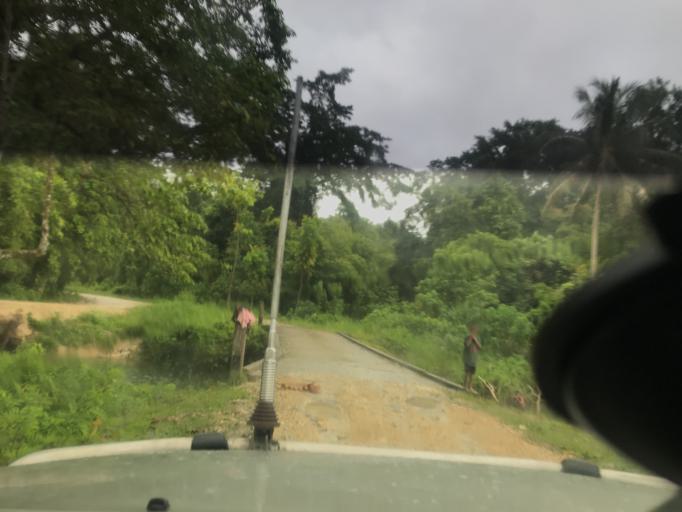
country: SB
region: Malaita
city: Auki
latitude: -9.0058
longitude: 160.8002
